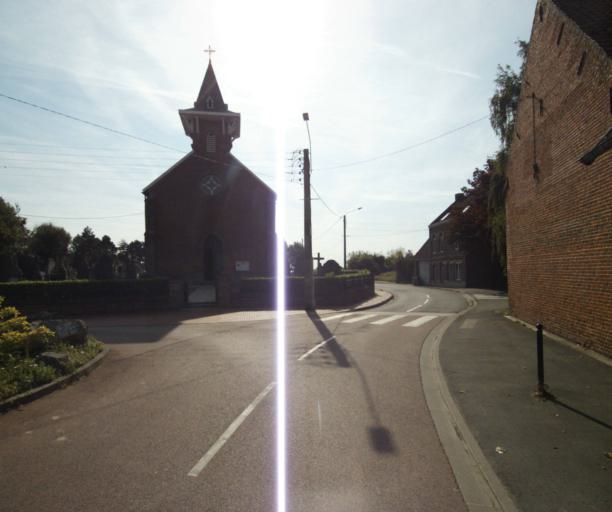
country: FR
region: Nord-Pas-de-Calais
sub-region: Departement du Nord
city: Capinghem
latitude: 50.6434
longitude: 2.9616
